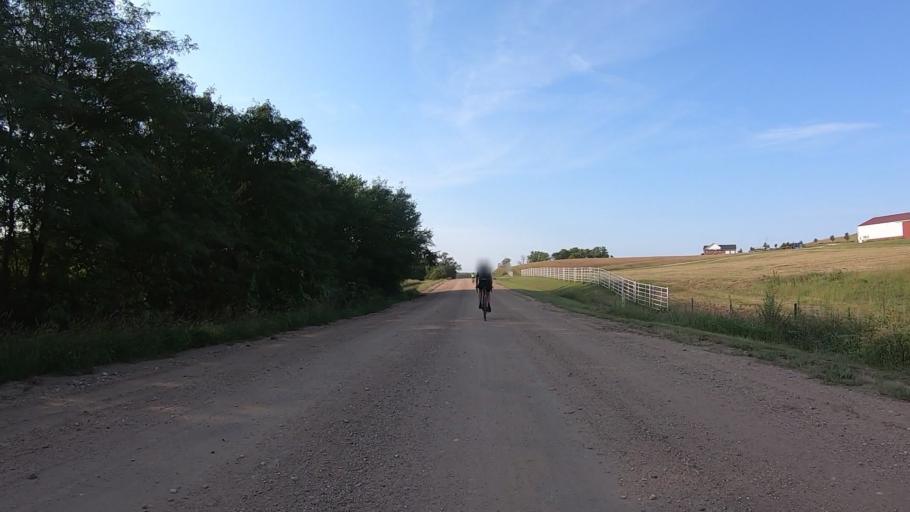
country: US
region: Kansas
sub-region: Marshall County
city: Blue Rapids
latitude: 39.6846
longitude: -96.7790
